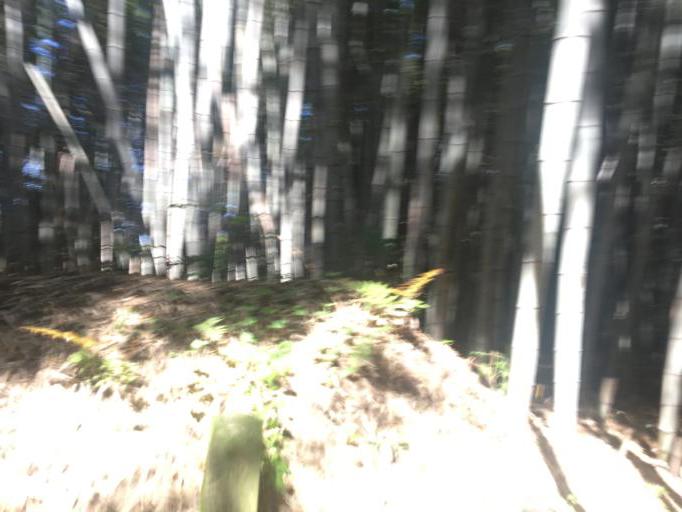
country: JP
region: Saitama
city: Shiki
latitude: 35.8620
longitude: 139.5883
